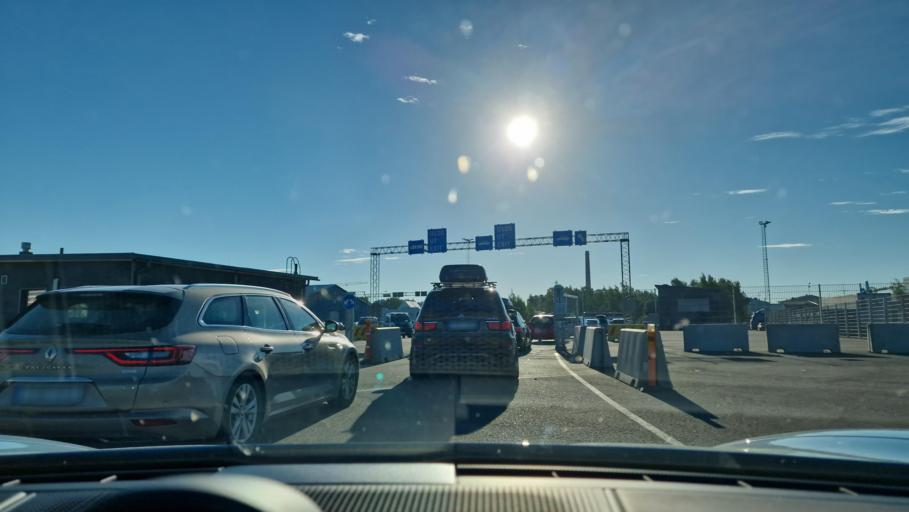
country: FI
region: Varsinais-Suomi
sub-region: Turku
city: Turku
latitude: 60.4379
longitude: 22.2227
